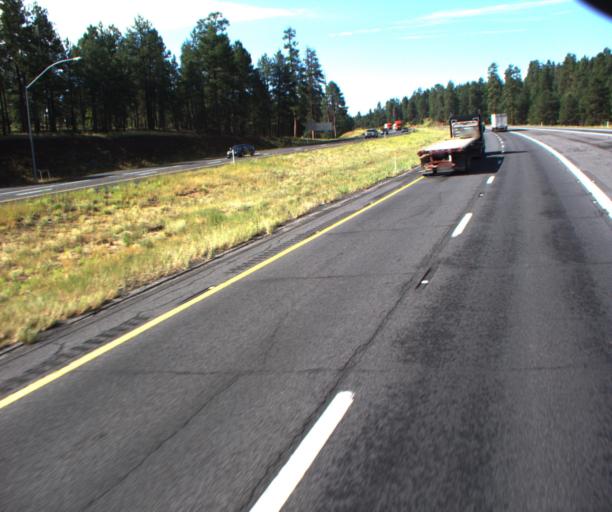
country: US
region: Arizona
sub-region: Coconino County
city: Kachina Village
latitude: 35.0865
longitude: -111.6873
